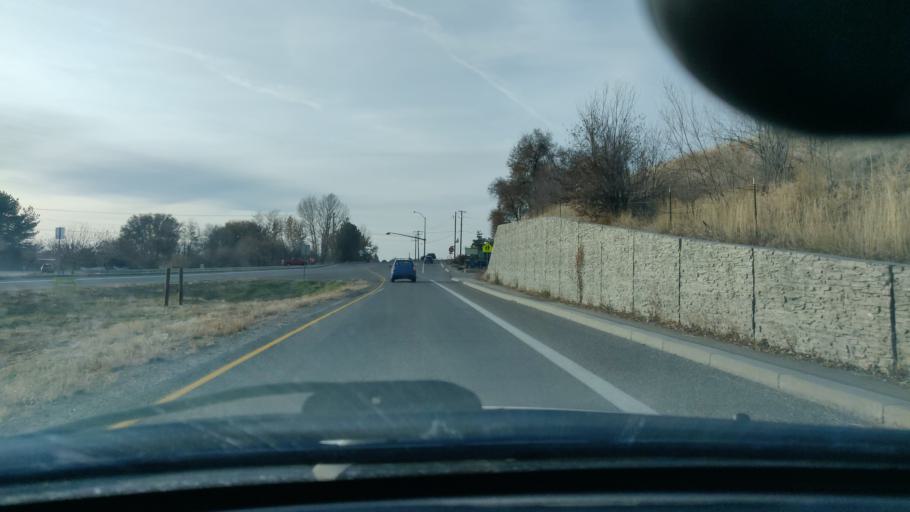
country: US
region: Idaho
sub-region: Ada County
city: Eagle
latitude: 43.6917
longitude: -116.3119
